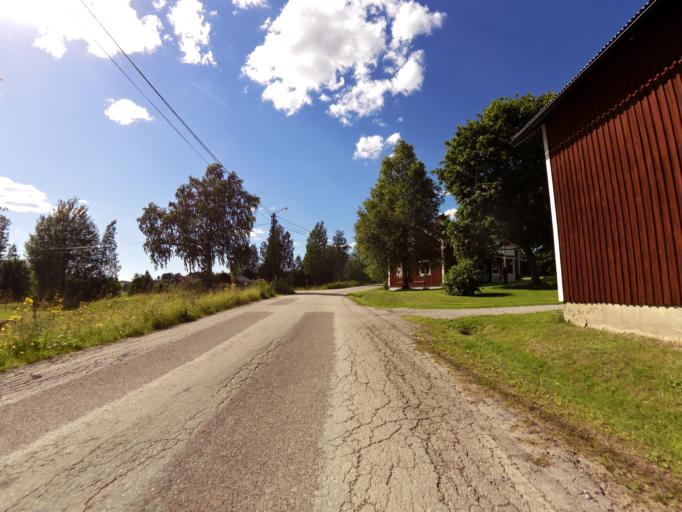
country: SE
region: Dalarna
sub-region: Faluns Kommun
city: Svardsjo
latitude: 60.6389
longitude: 15.8558
